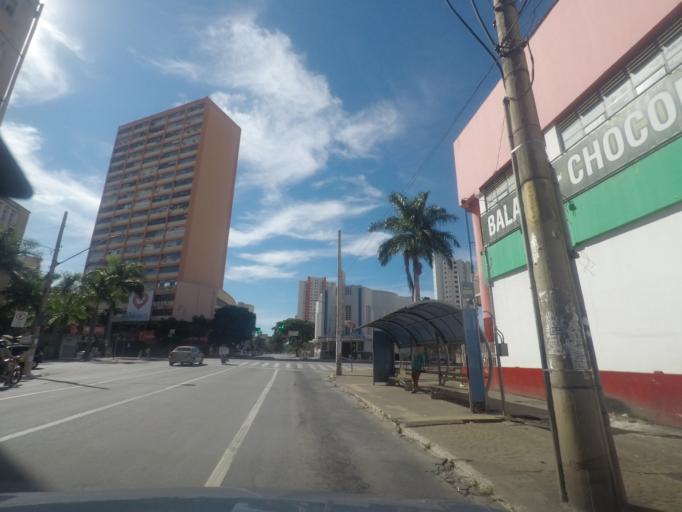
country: BR
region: Goias
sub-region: Goiania
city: Goiania
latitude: -16.6757
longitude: -49.2618
